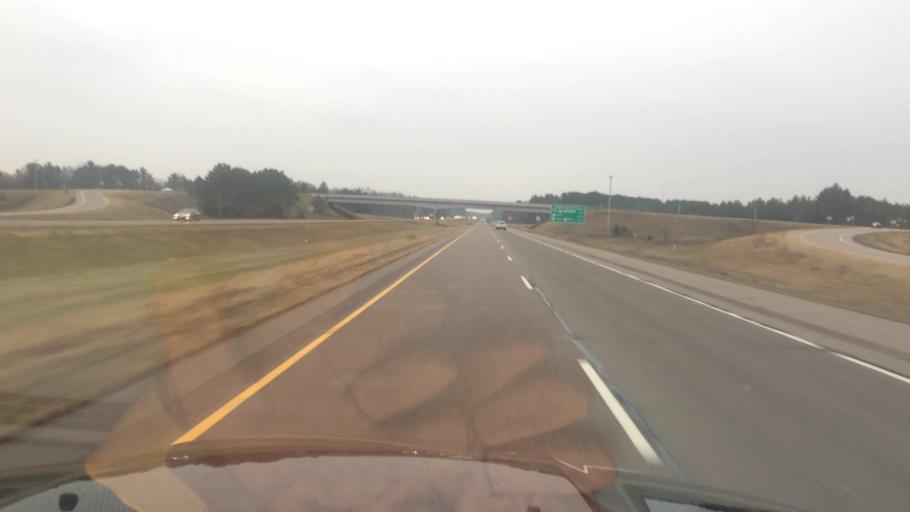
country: US
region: Wisconsin
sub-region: Portage County
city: Stevens Point
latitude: 44.5723
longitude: -89.6004
